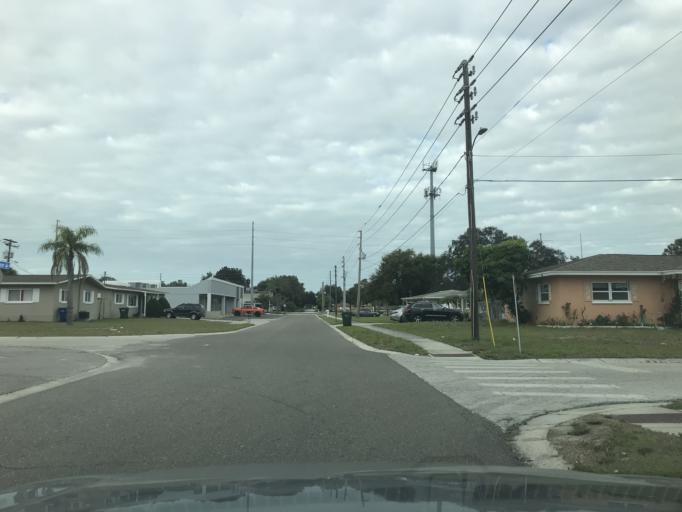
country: US
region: Florida
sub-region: Pinellas County
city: Belleair
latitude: 27.9334
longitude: -82.7857
